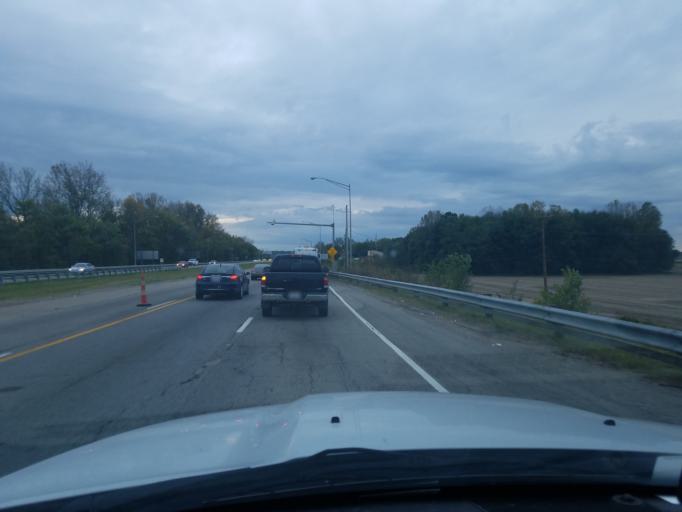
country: US
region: Indiana
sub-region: Vanderburgh County
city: Evansville
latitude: 37.9294
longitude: -87.5484
